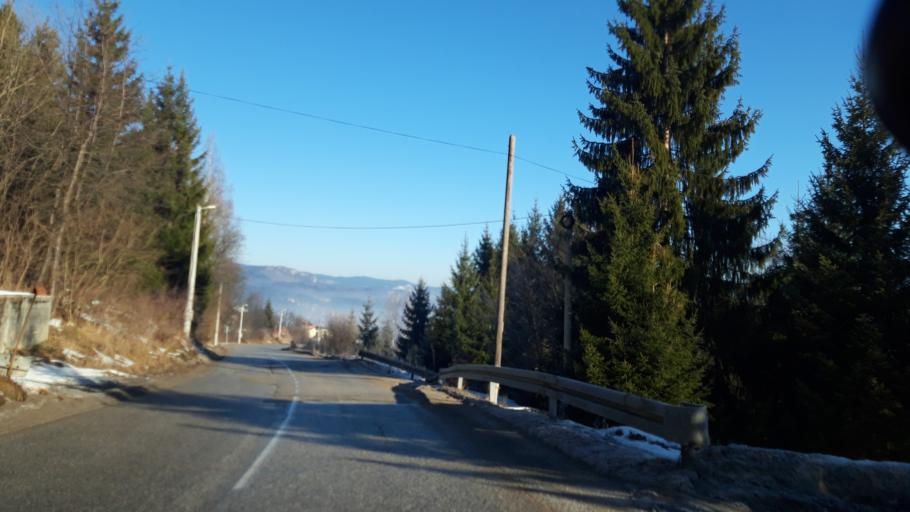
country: BA
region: Republika Srpska
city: Koran
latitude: 43.8055
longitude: 18.5535
